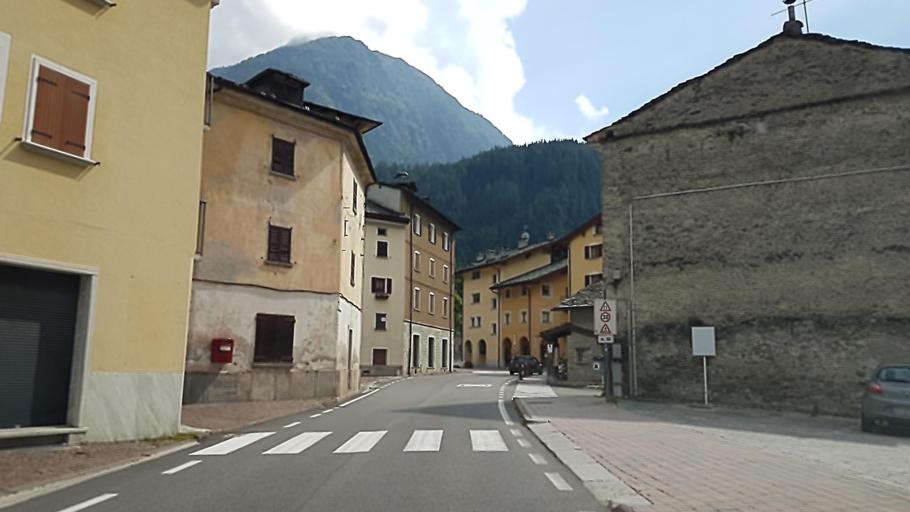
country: IT
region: Lombardy
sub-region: Provincia di Sondrio
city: Campodolcino
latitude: 46.4068
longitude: 9.3516
